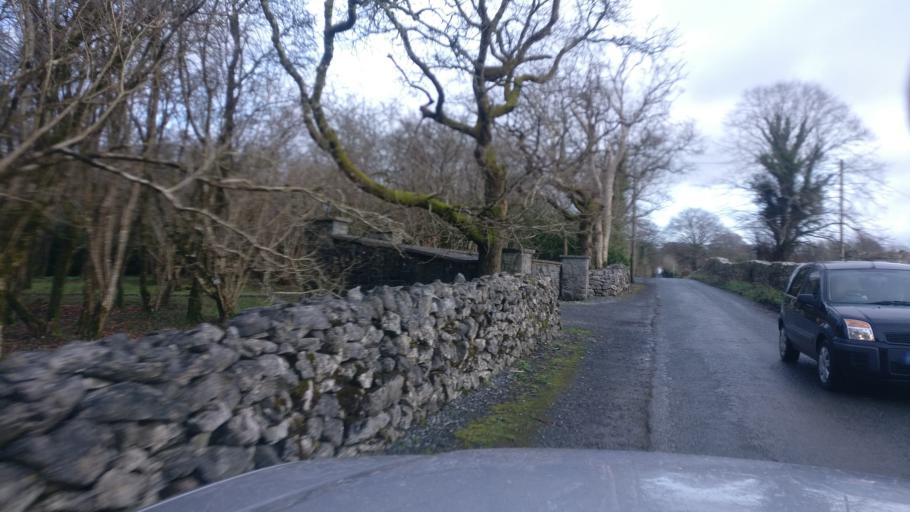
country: IE
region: Connaught
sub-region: County Galway
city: Athenry
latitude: 53.2609
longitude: -8.7058
